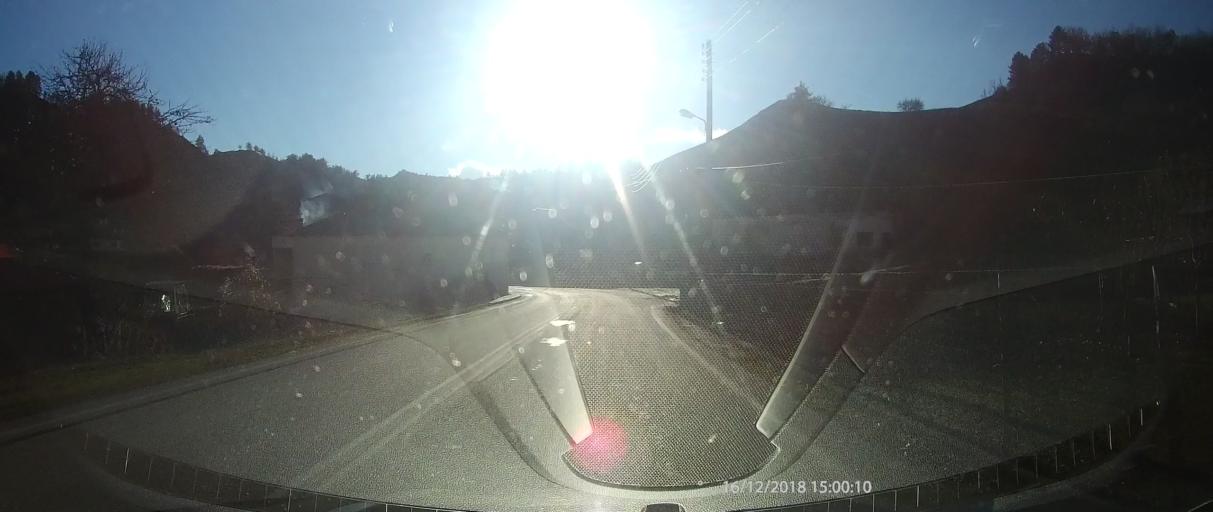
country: GR
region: West Macedonia
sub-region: Nomos Kastorias
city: Nestorio
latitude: 40.2213
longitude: 21.0188
